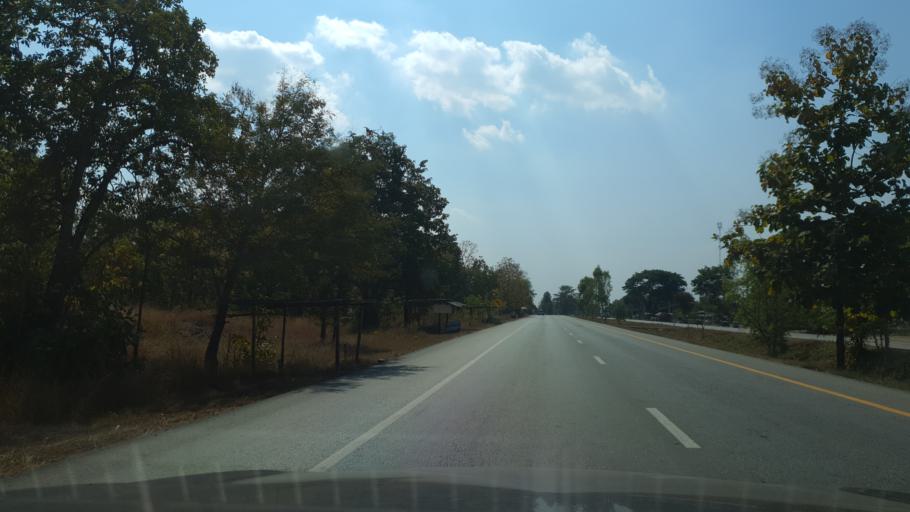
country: TH
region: Tak
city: Sam Ngao
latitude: 17.2994
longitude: 99.1452
